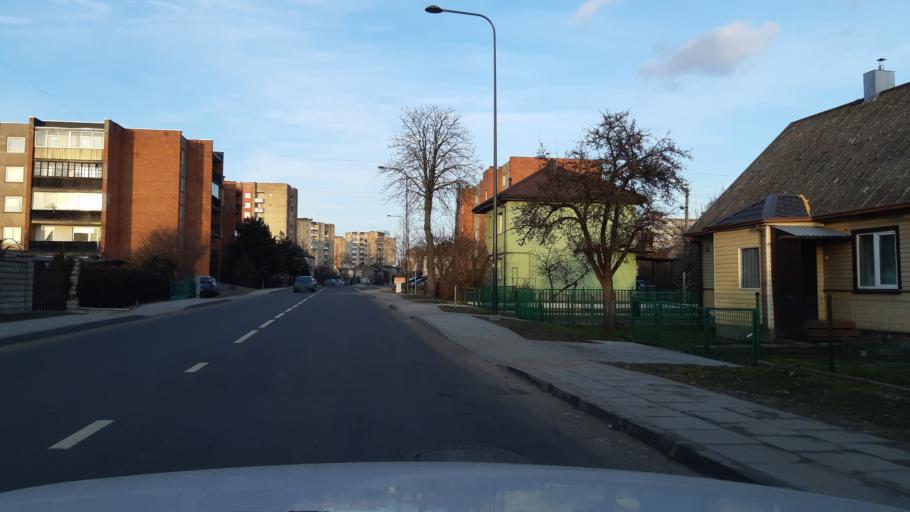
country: LT
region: Kauno apskritis
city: Dainava (Kaunas)
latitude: 54.8889
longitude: 23.9430
